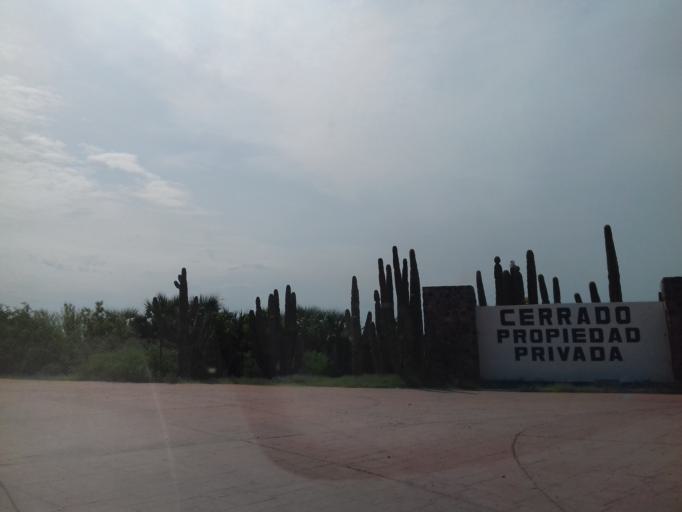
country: MX
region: Sonora
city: Heroica Guaymas
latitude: 27.9736
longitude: -111.1116
